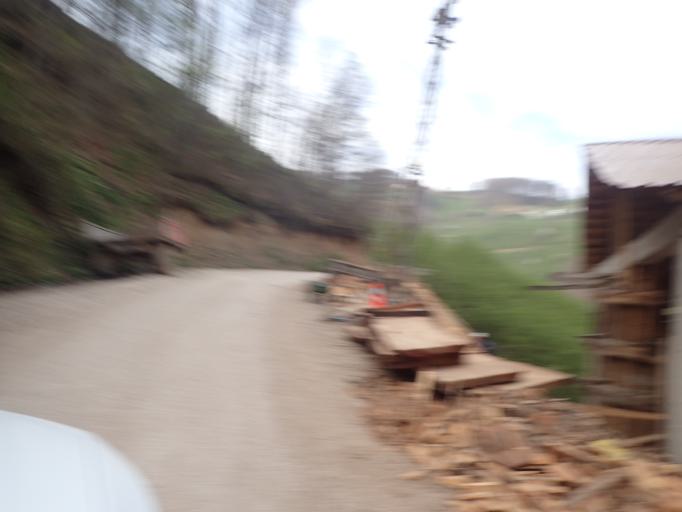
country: TR
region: Ordu
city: Aybasti
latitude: 40.7012
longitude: 37.2808
